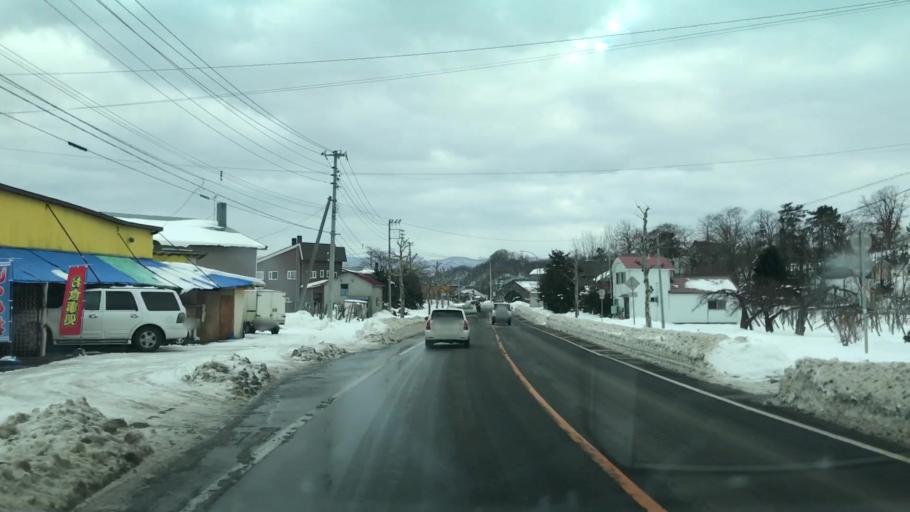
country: JP
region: Hokkaido
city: Yoichi
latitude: 43.2091
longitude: 140.7651
